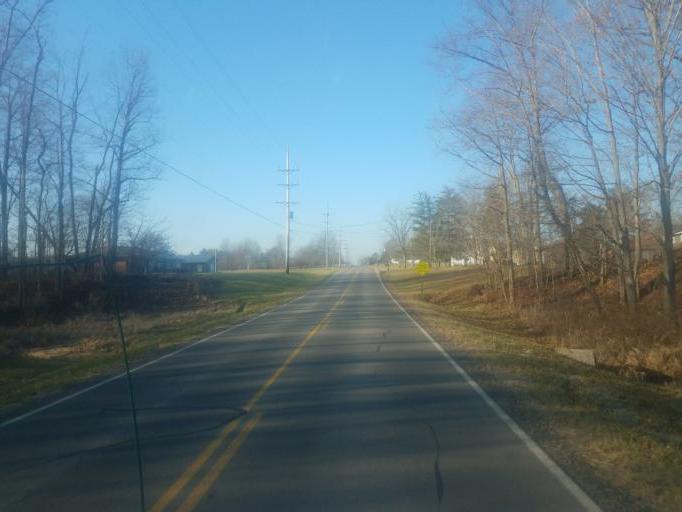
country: US
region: Ohio
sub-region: Crawford County
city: Bucyrus
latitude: 40.8303
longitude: -82.8869
